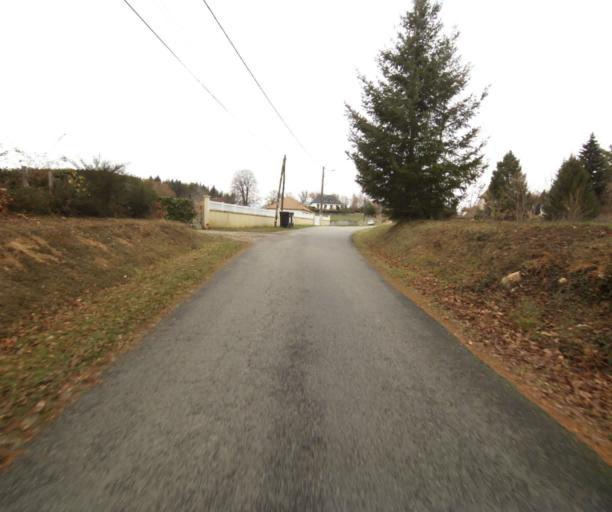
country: FR
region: Limousin
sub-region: Departement de la Correze
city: Saint-Mexant
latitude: 45.2603
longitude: 1.6632
